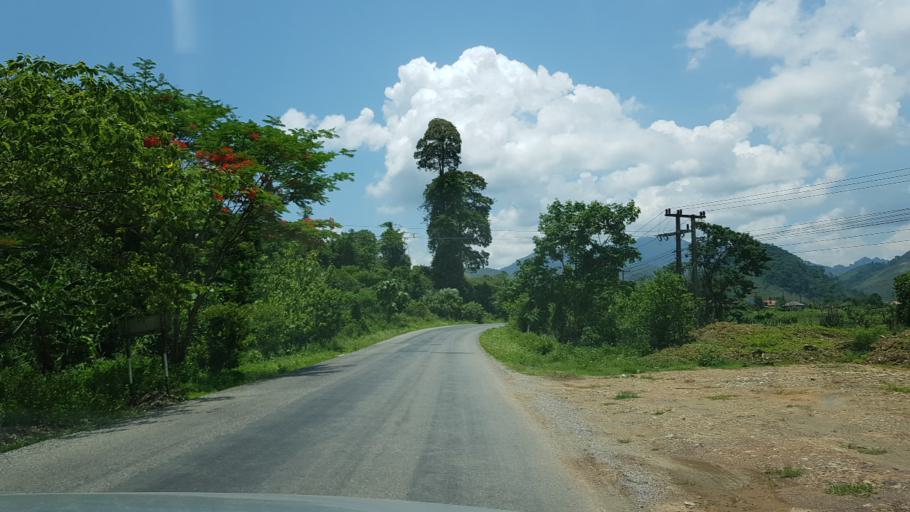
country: LA
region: Vientiane
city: Muang Kasi
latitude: 19.1270
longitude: 102.2614
